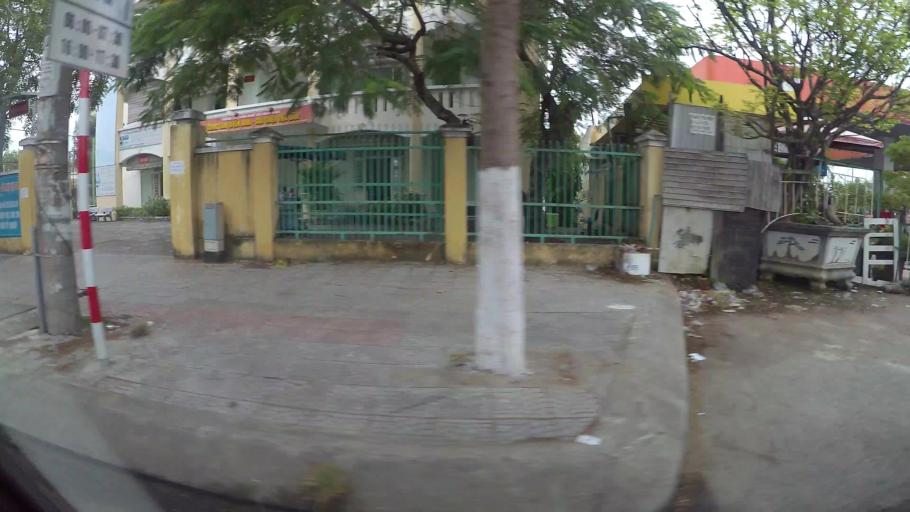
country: VN
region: Da Nang
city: Son Tra
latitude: 16.0454
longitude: 108.2398
